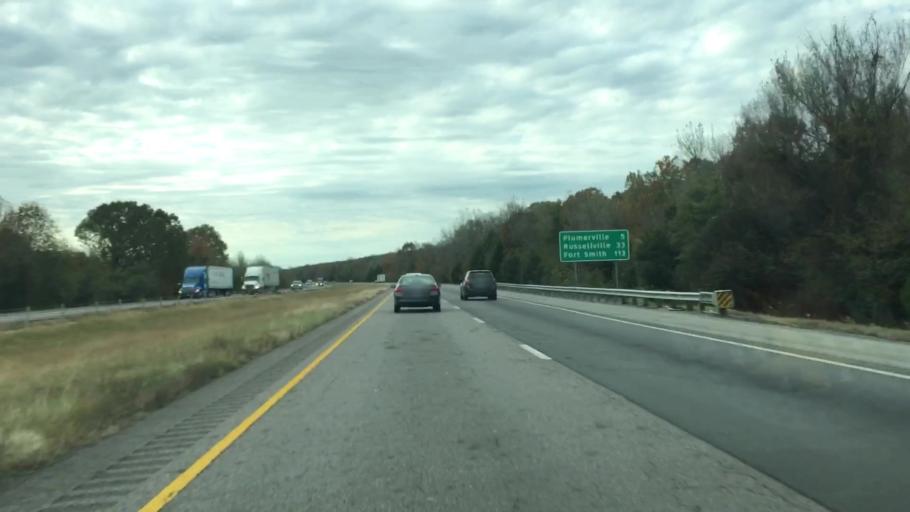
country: US
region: Arkansas
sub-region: Faulkner County
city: Conway
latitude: 35.1567
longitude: -92.5653
